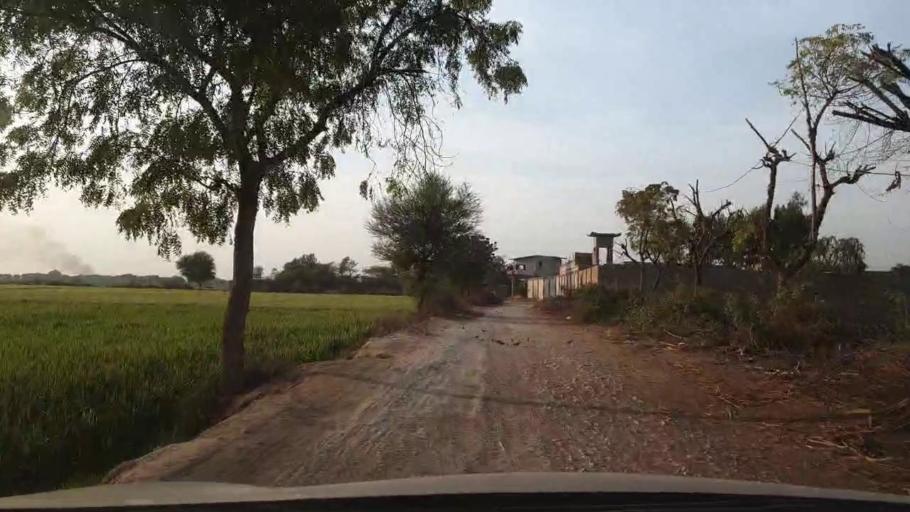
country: PK
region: Sindh
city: Tando Adam
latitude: 25.7122
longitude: 68.7230
